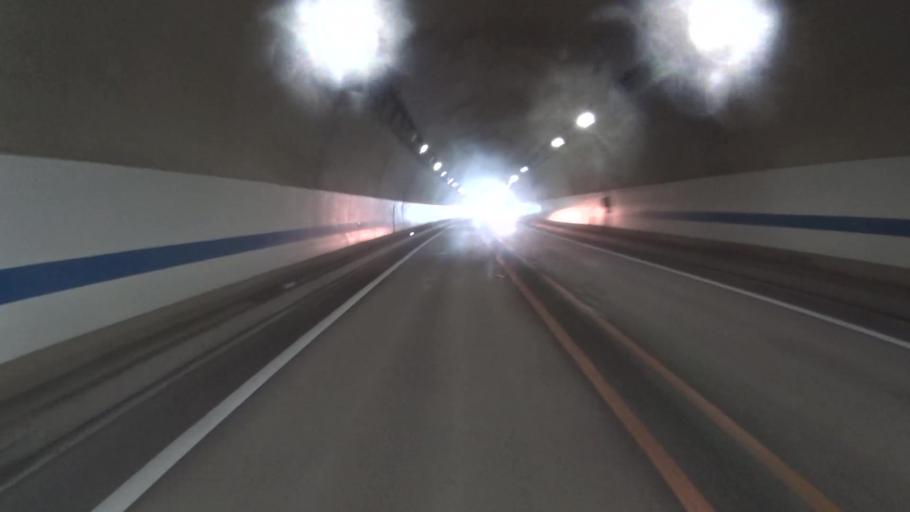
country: JP
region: Kyoto
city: Ayabe
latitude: 35.3759
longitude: 135.2652
